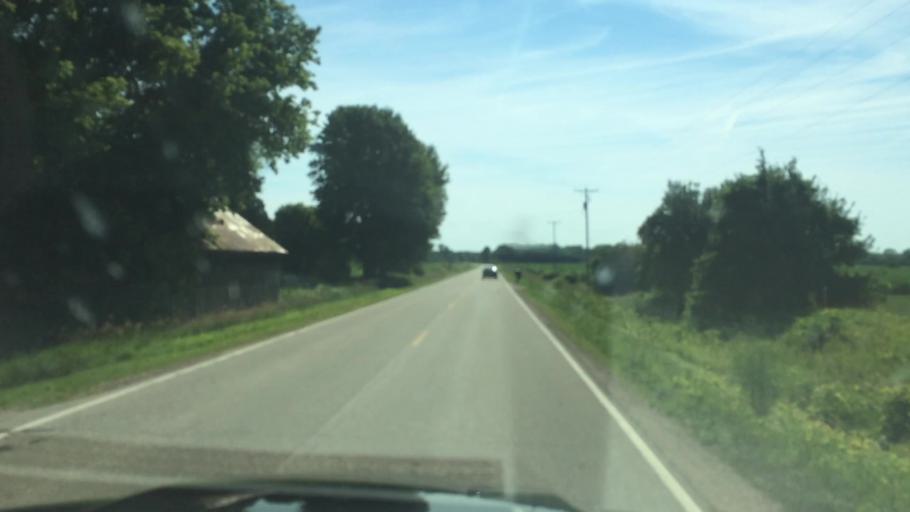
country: US
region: Wisconsin
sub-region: Oconto County
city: Gillett
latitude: 44.7876
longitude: -88.3213
